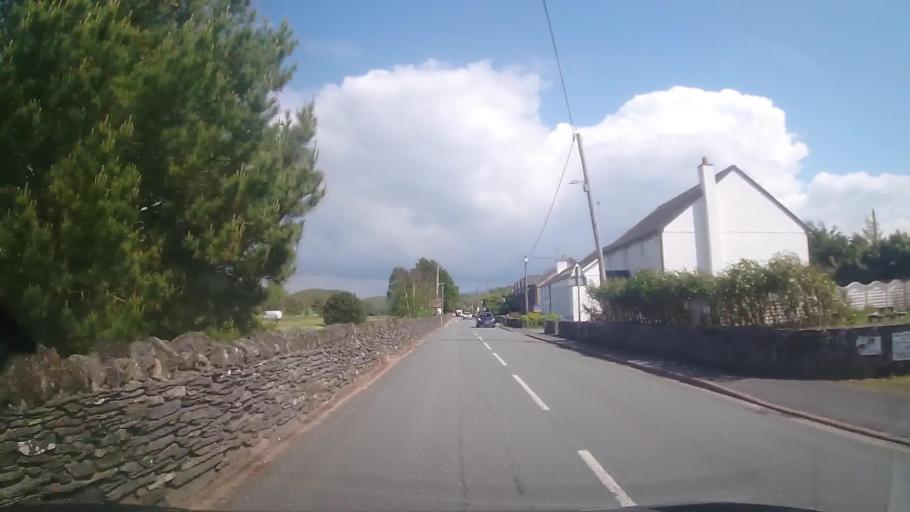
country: GB
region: Wales
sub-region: Gwynedd
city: Porthmadog
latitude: 52.9136
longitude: -4.1654
